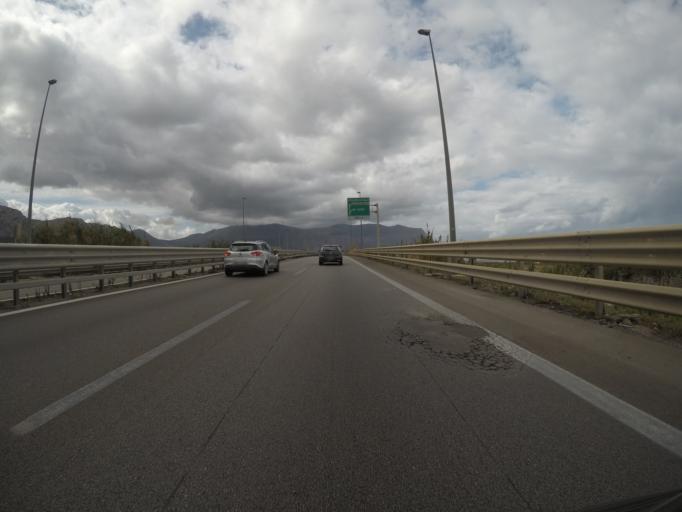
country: IT
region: Sicily
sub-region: Palermo
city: Capaci
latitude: 38.1784
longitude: 13.2267
